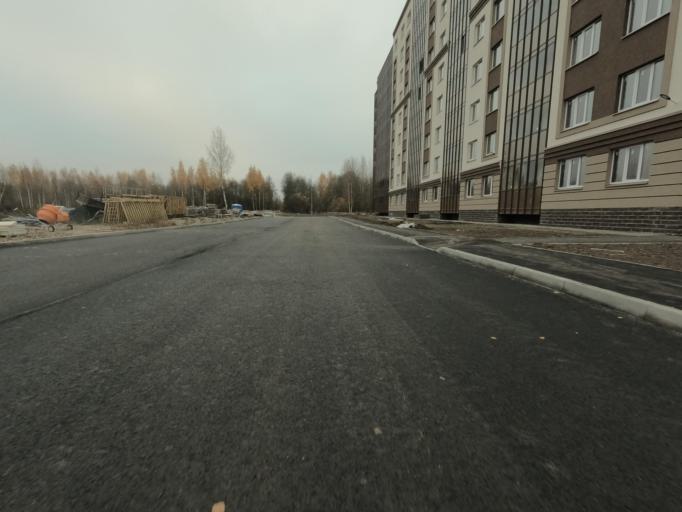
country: RU
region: Leningrad
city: Kirovsk
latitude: 59.8792
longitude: 31.0092
